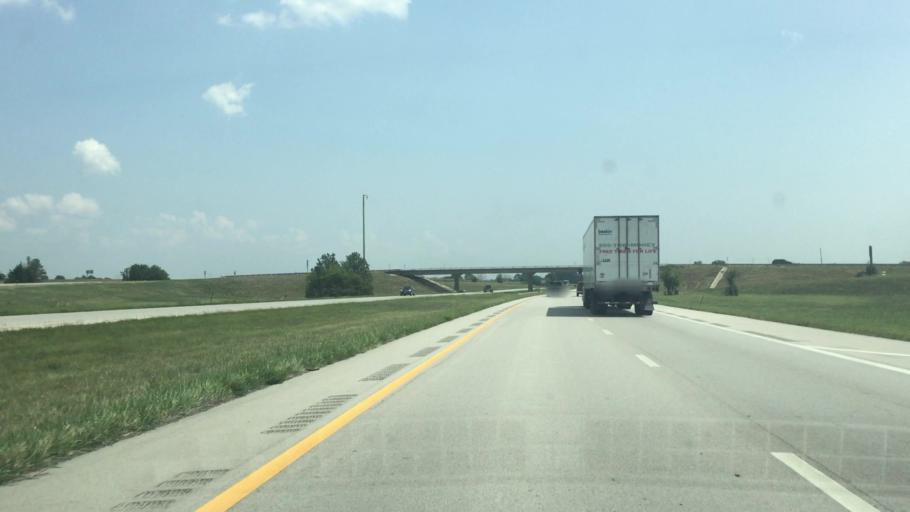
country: US
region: Kansas
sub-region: Johnson County
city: Edgerton
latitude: 38.7455
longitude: -95.0035
